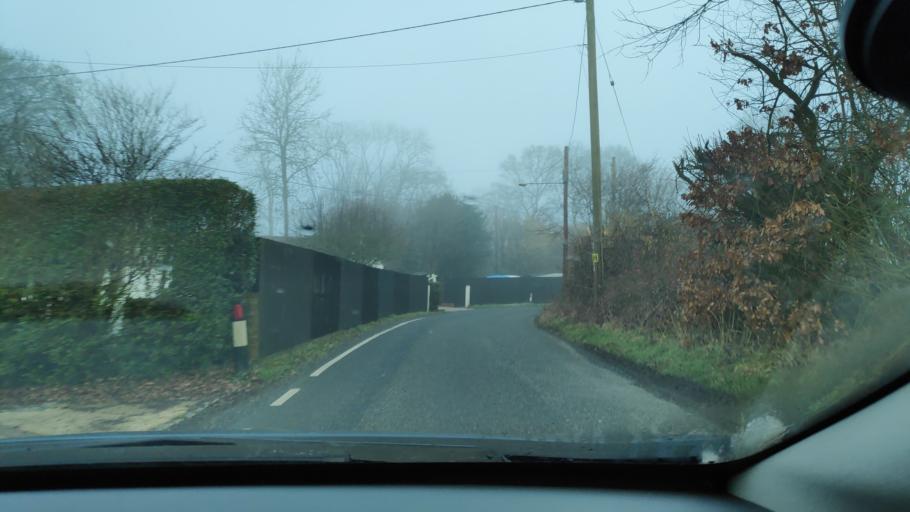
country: GB
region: England
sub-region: Surrey
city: Seale
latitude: 51.2469
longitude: -0.7048
